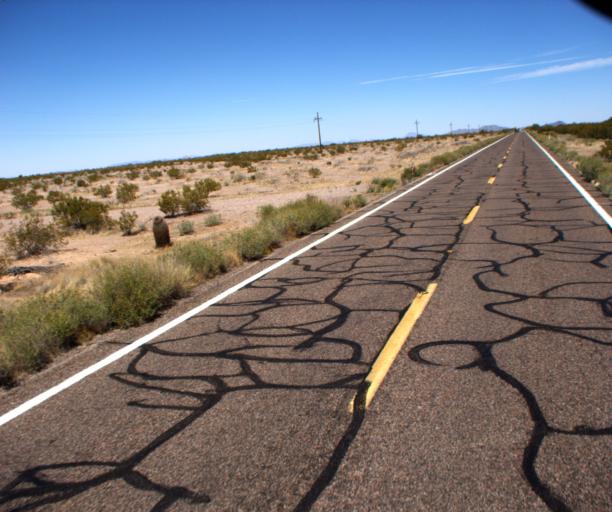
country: US
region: Arizona
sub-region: Pima County
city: Ajo
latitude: 32.6022
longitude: -112.8700
